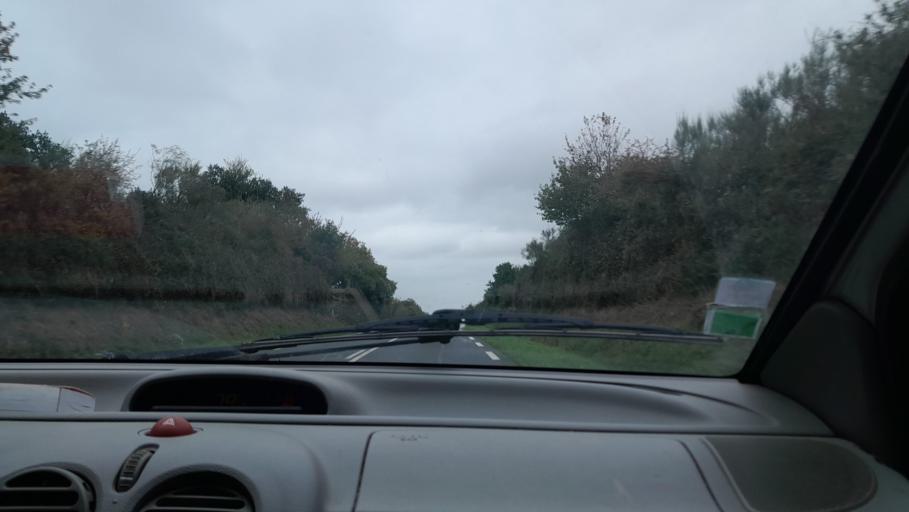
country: FR
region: Pays de la Loire
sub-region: Departement de la Loire-Atlantique
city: Saint-Mars-la-Jaille
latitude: 47.5433
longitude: -1.1863
